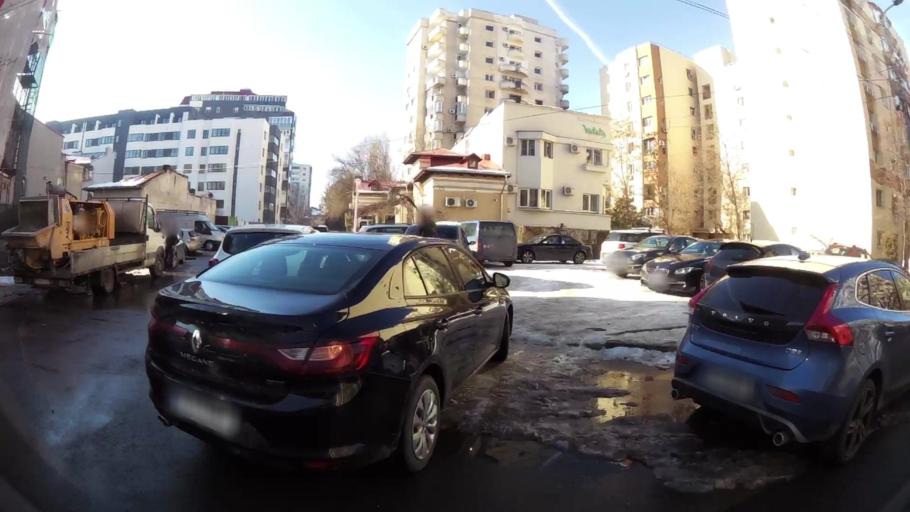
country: RO
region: Bucuresti
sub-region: Municipiul Bucuresti
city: Bucharest
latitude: 44.4307
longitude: 26.1326
